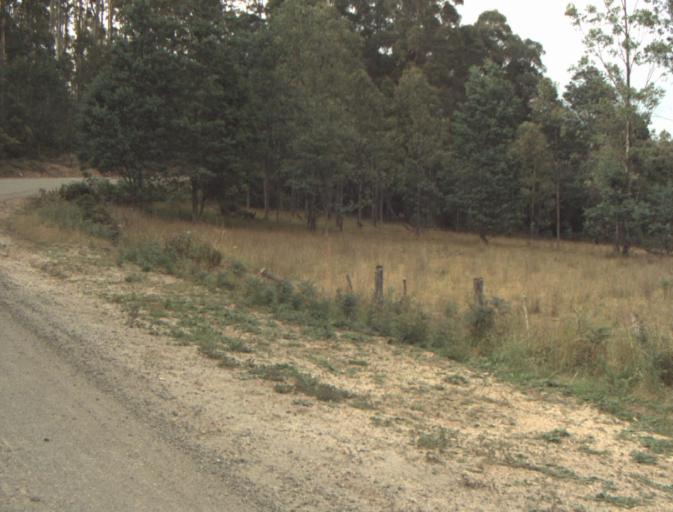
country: AU
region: Tasmania
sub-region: Dorset
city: Scottsdale
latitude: -41.3359
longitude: 147.4340
